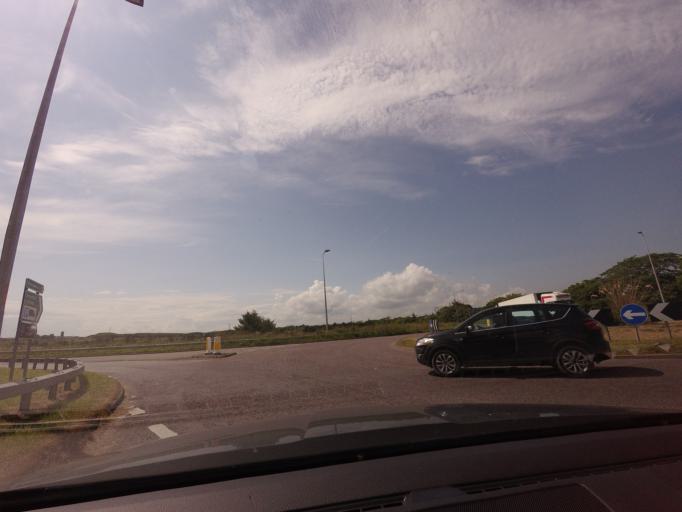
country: GB
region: Scotland
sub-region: Aberdeenshire
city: Peterhead
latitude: 57.5072
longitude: -1.8258
